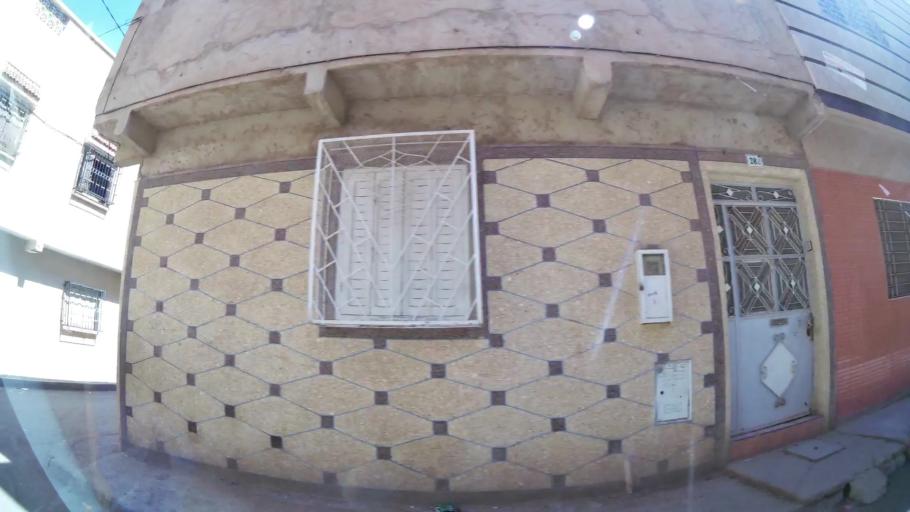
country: MA
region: Oriental
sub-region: Oujda-Angad
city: Oujda
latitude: 34.6561
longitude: -1.9023
